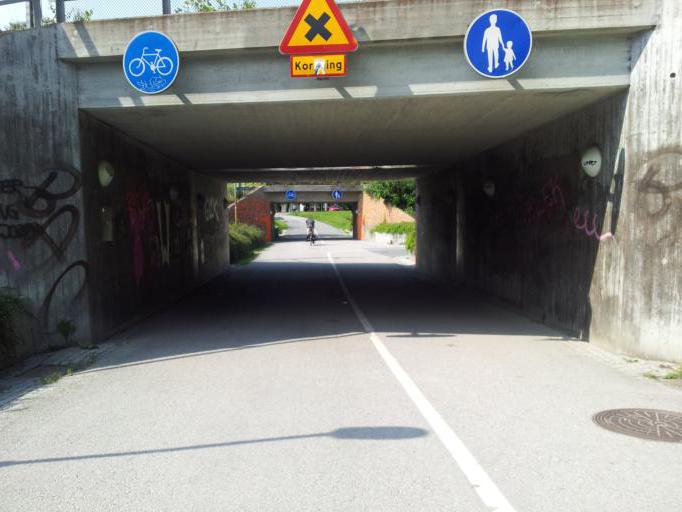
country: SE
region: Uppsala
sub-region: Uppsala Kommun
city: Uppsala
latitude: 59.8644
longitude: 17.6370
